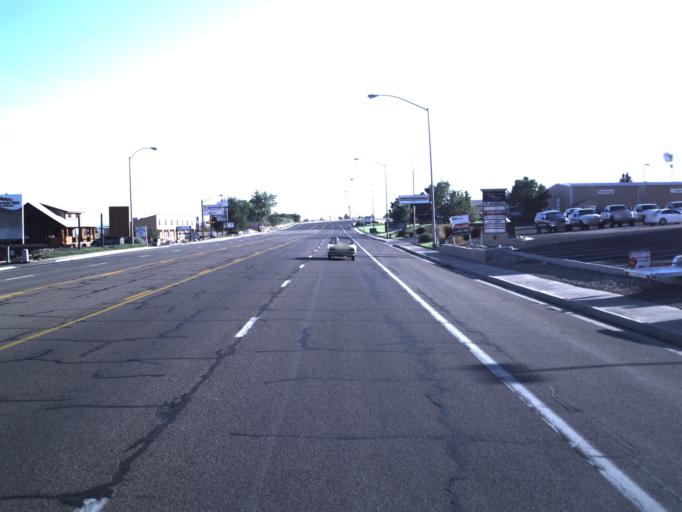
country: US
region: Utah
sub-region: Iron County
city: Cedar City
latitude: 37.7136
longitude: -113.0605
